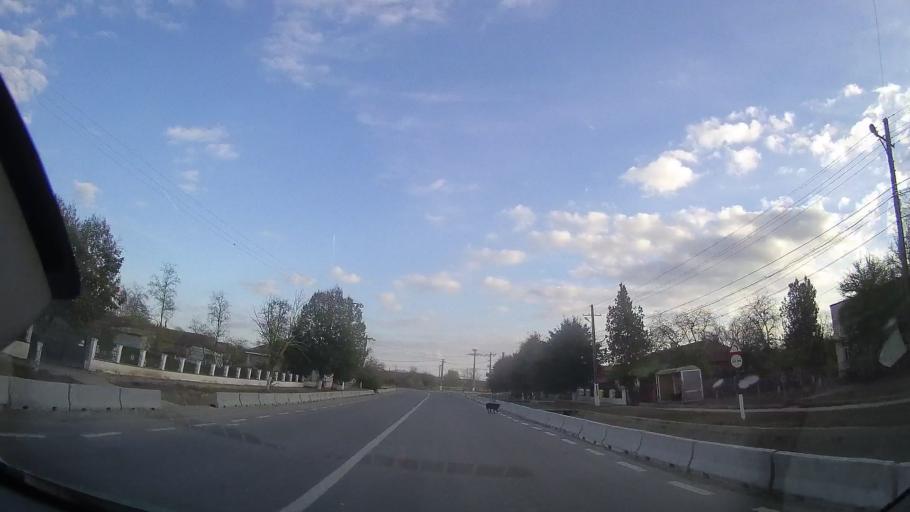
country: RO
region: Constanta
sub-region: Comuna Independenta
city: Independenta
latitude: 43.9495
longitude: 28.0853
